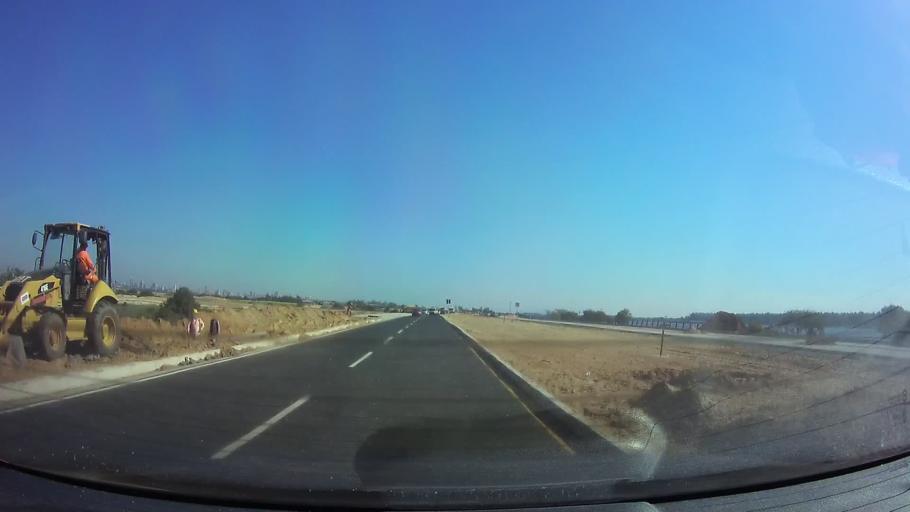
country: PY
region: Asuncion
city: Asuncion
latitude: -25.2454
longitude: -57.5922
